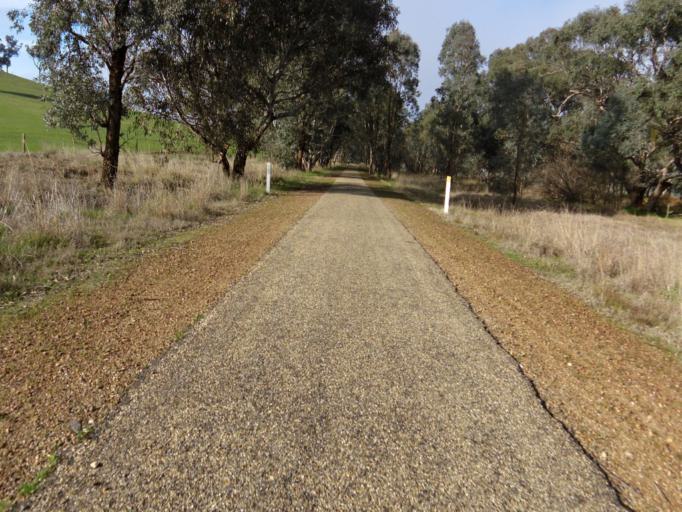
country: AU
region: Victoria
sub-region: Wangaratta
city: Wangaratta
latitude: -36.4462
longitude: 146.5512
